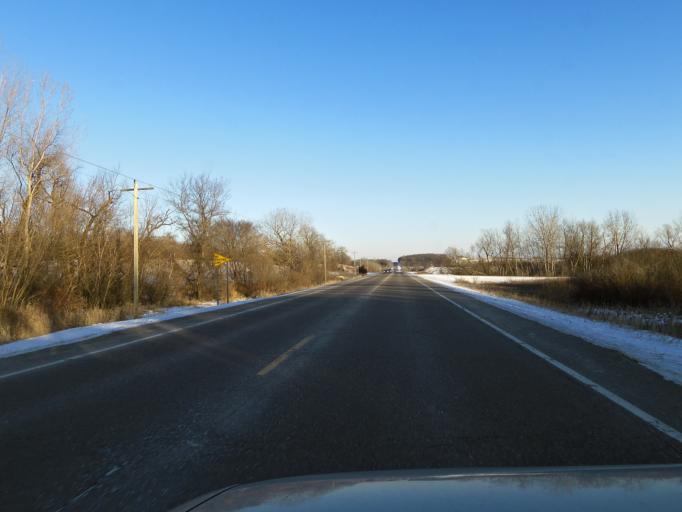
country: US
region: Minnesota
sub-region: Scott County
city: Elko New Market
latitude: 44.5439
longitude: -93.2430
